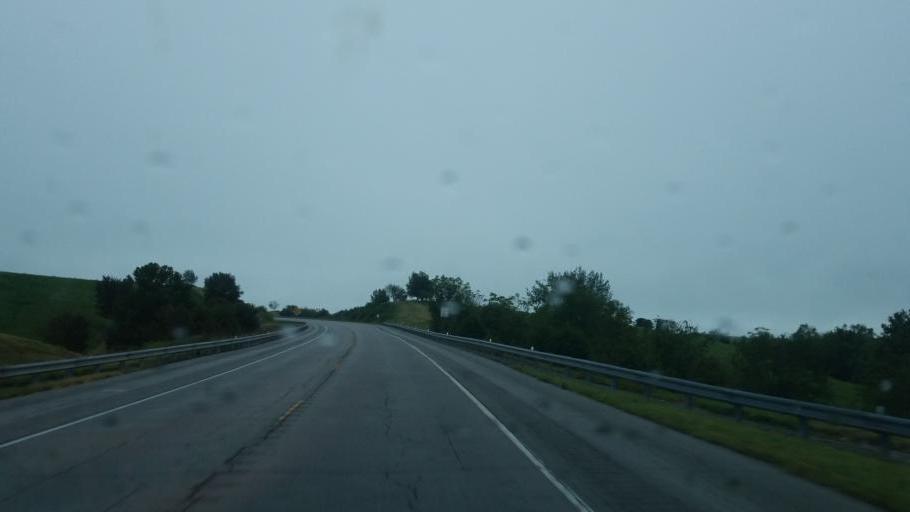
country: US
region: Kentucky
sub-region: Fleming County
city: Flemingsburg
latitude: 38.3988
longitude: -83.7206
